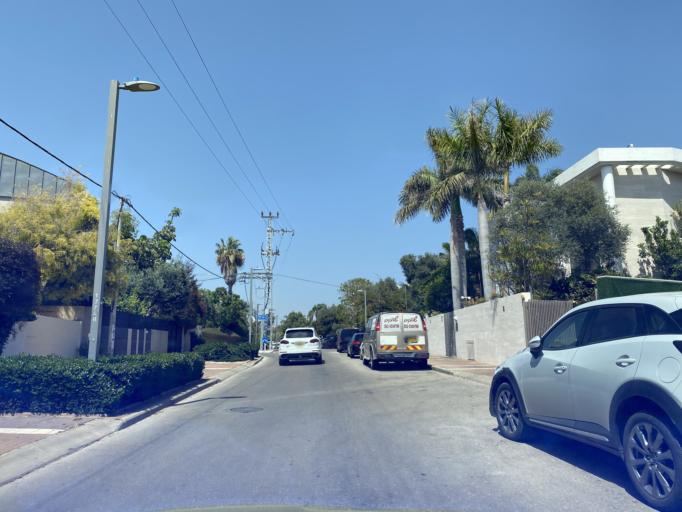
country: IL
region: Tel Aviv
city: Herzliya Pituah
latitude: 32.1743
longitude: 34.8133
